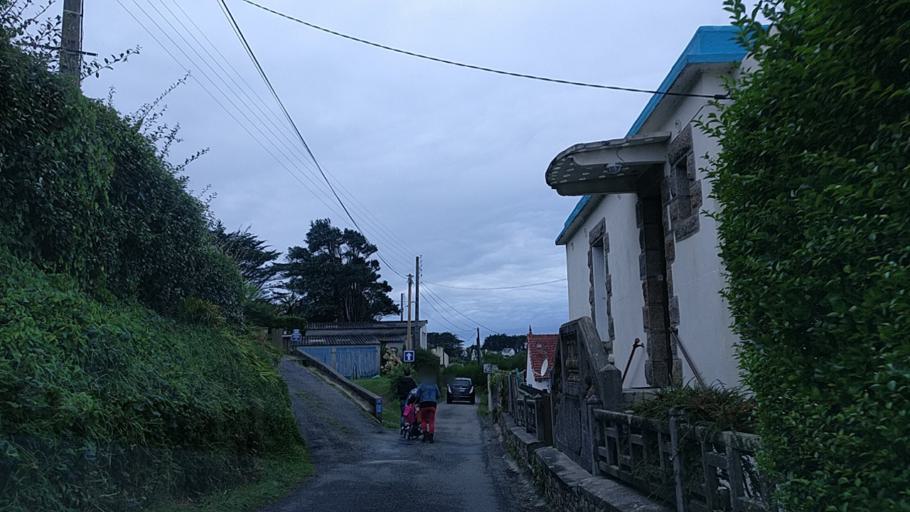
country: FR
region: Brittany
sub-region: Departement du Finistere
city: Saint-Pabu
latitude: 48.5721
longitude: -4.6068
